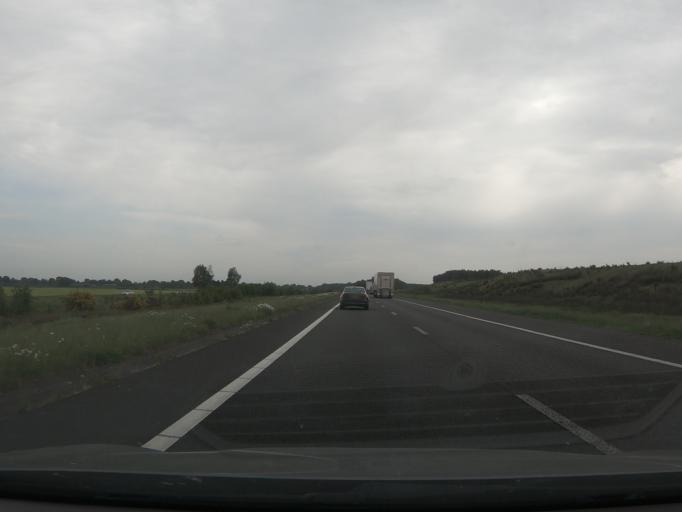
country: NL
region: Drenthe
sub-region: Gemeente Hoogeveen
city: Hoogeveen
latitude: 52.8083
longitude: 6.4589
